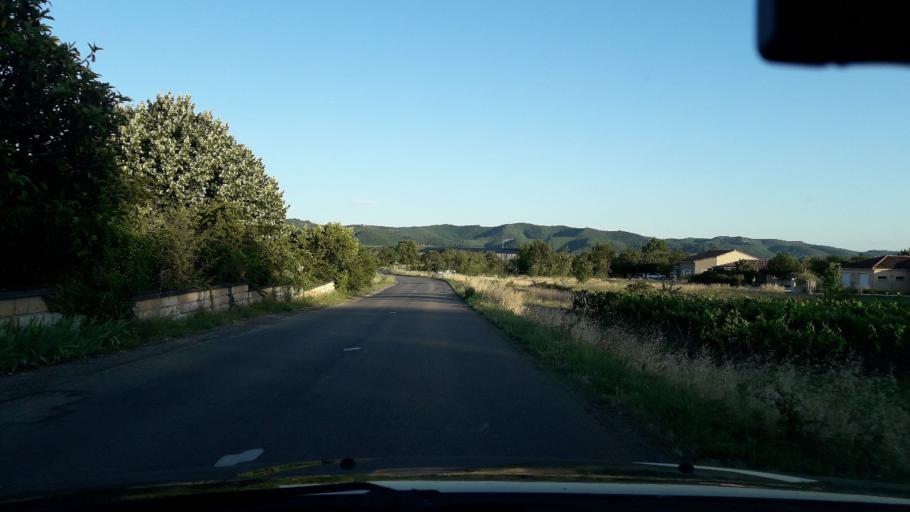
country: FR
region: Rhone-Alpes
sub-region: Departement de l'Ardeche
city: Lavilledieu
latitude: 44.5867
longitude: 4.4609
